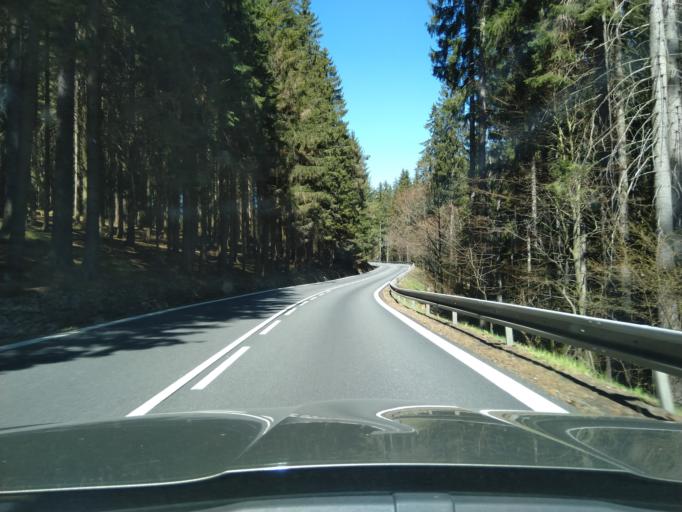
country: CZ
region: Jihocesky
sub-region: Okres Prachatice
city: Vimperk
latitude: 49.0002
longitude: 13.7686
